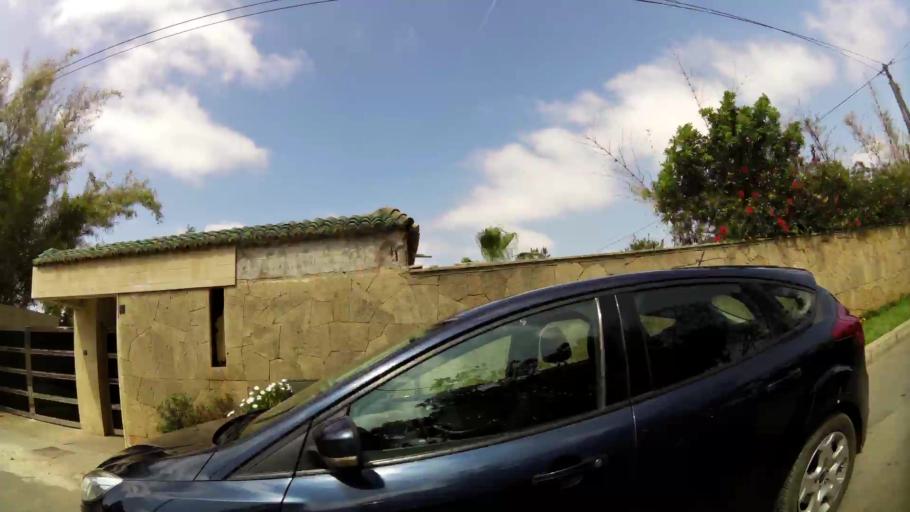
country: MA
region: Rabat-Sale-Zemmour-Zaer
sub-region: Rabat
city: Rabat
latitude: 33.9813
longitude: -6.8388
